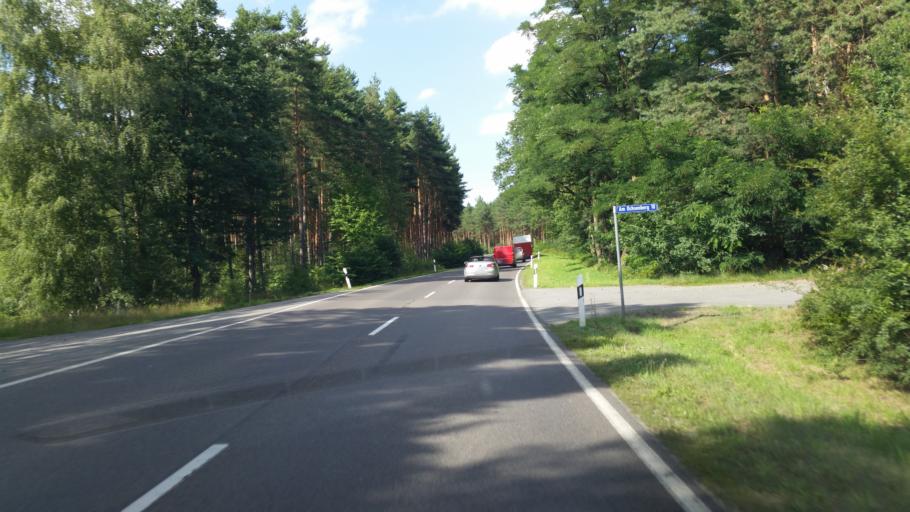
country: DE
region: Saxony
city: Kamenz
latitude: 51.3071
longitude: 14.0932
